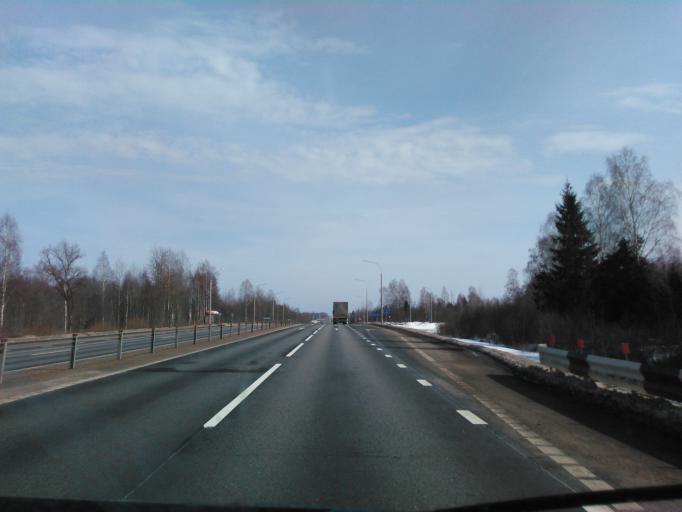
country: BY
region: Vitebsk
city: Dubrowna
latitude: 54.6899
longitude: 30.9286
